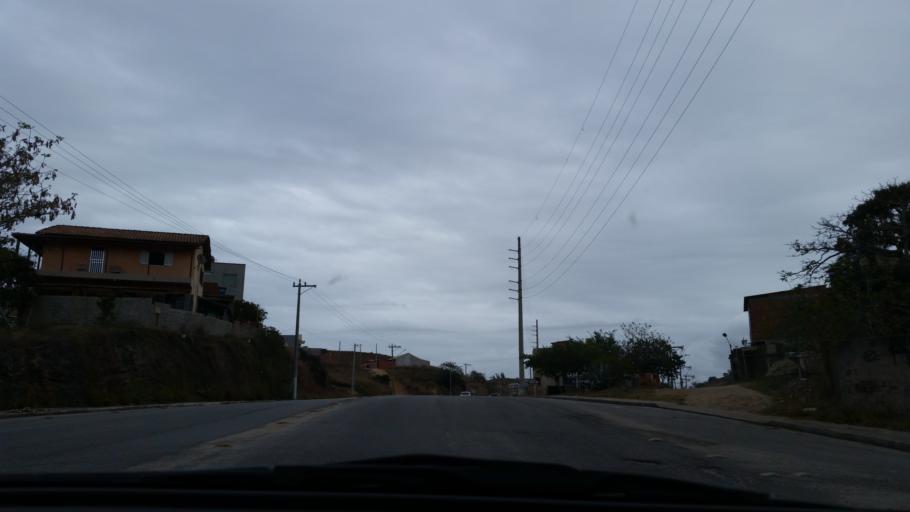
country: BR
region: Rio de Janeiro
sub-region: Cabo Frio
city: Cabo Frio
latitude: -22.8550
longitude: -42.0475
